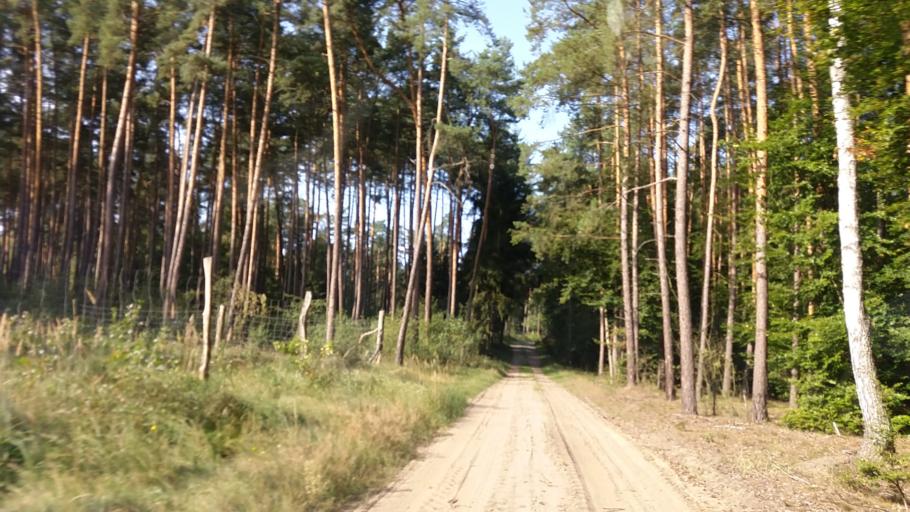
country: PL
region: West Pomeranian Voivodeship
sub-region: Powiat choszczenski
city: Choszczno
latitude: 53.2432
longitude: 15.4049
